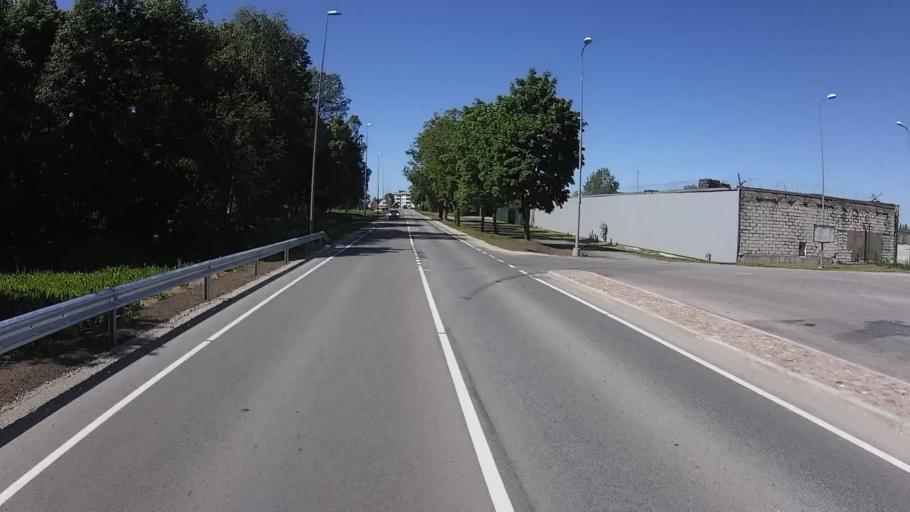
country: EE
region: Ida-Virumaa
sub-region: Johvi vald
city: Johvi
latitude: 59.3497
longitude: 27.4337
